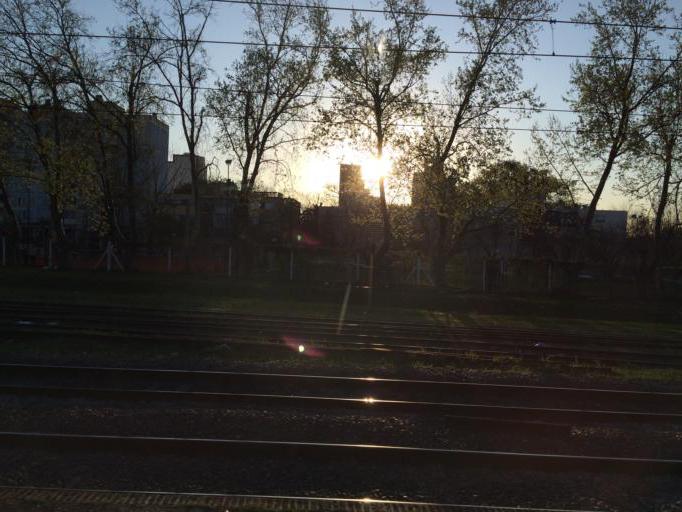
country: AR
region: Buenos Aires
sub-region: Partido de Lanus
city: Lanus
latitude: -34.7255
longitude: -58.3935
